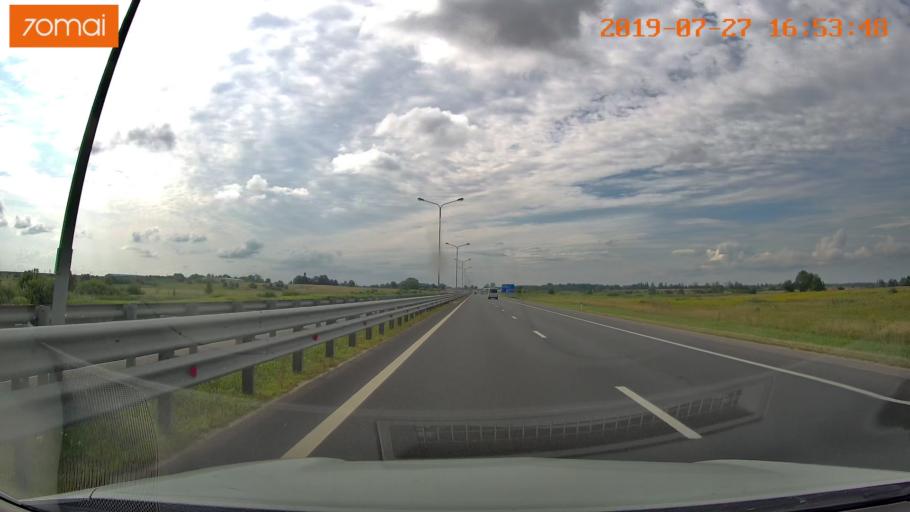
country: RU
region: Kaliningrad
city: Bol'shoe Isakovo
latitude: 54.6903
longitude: 20.8245
